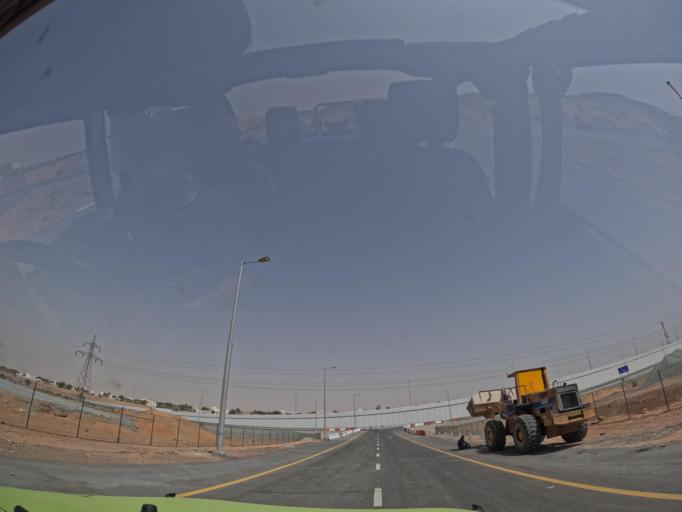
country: OM
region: Al Buraimi
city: Al Buraymi
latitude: 24.7393
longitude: 55.7982
